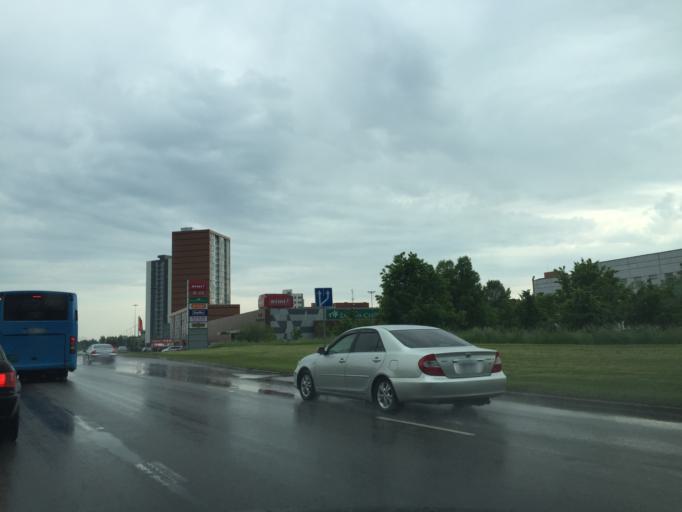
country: LT
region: Klaipedos apskritis
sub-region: Klaipeda
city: Klaipeda
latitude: 55.7531
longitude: 21.1303
